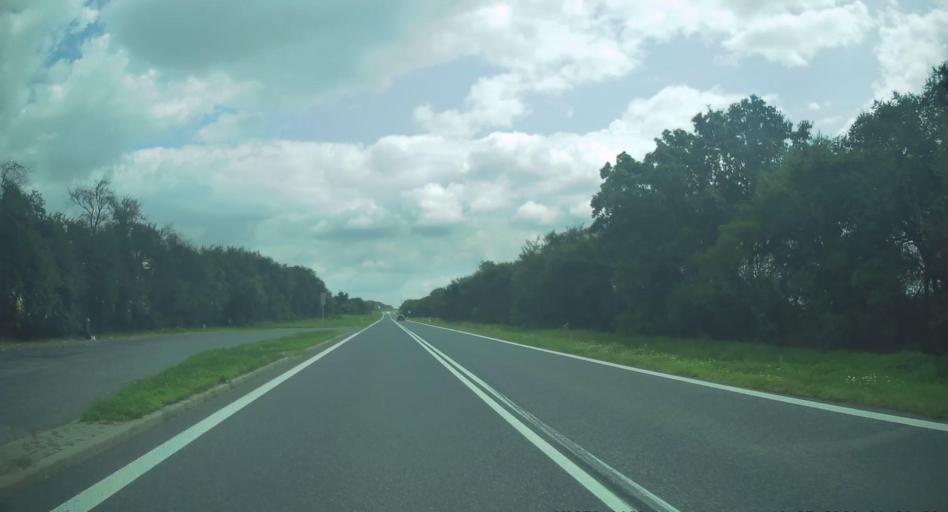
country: PL
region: Opole Voivodeship
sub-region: Powiat prudnicki
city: Lubrza
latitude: 50.3326
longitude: 17.6847
